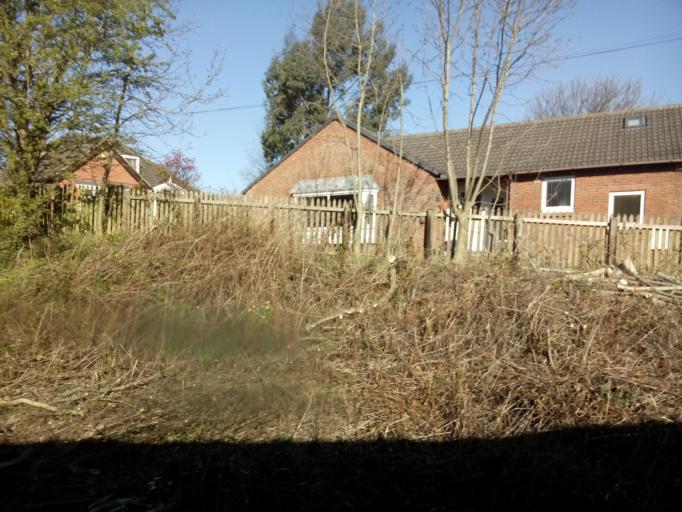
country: GB
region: England
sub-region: Northumberland
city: Morpeth
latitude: 55.1610
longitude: -1.6860
